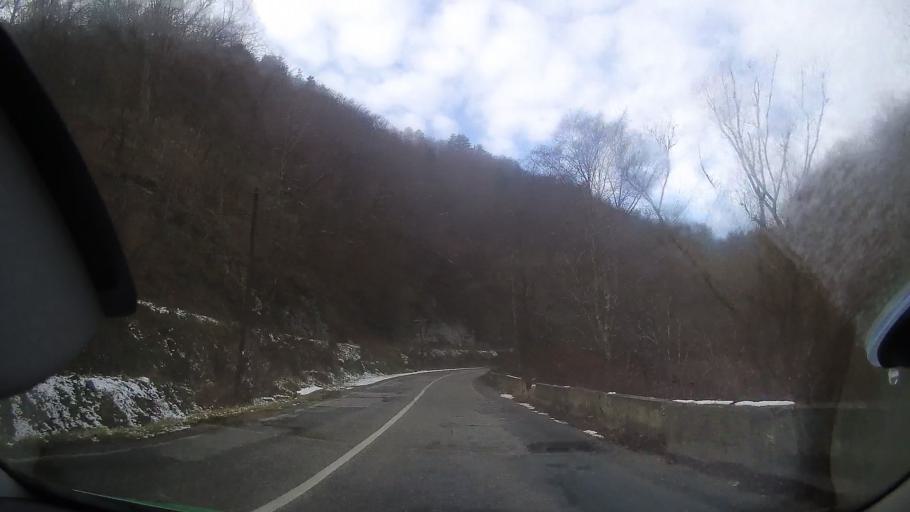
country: RO
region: Alba
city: Salciua de Sus
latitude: 46.4148
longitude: 23.4598
